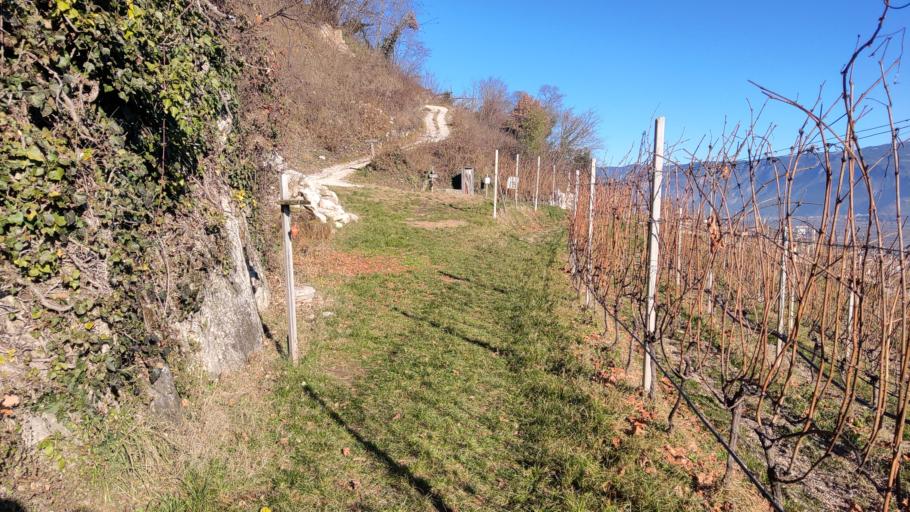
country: IT
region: Trentino-Alto Adige
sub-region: Bolzano
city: Cortaccia sulla Strada del Vino
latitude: 46.3054
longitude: 11.2135
